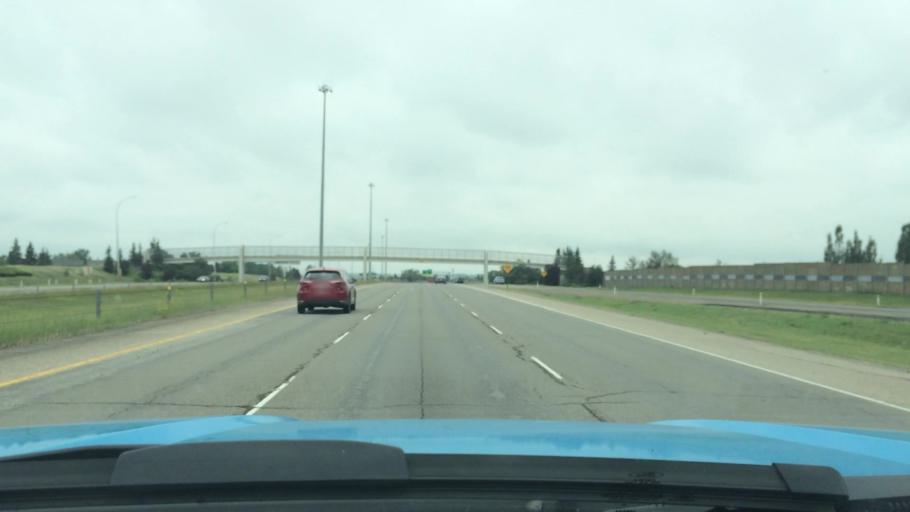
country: CA
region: Alberta
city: Airdrie
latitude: 51.2855
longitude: -114.0012
